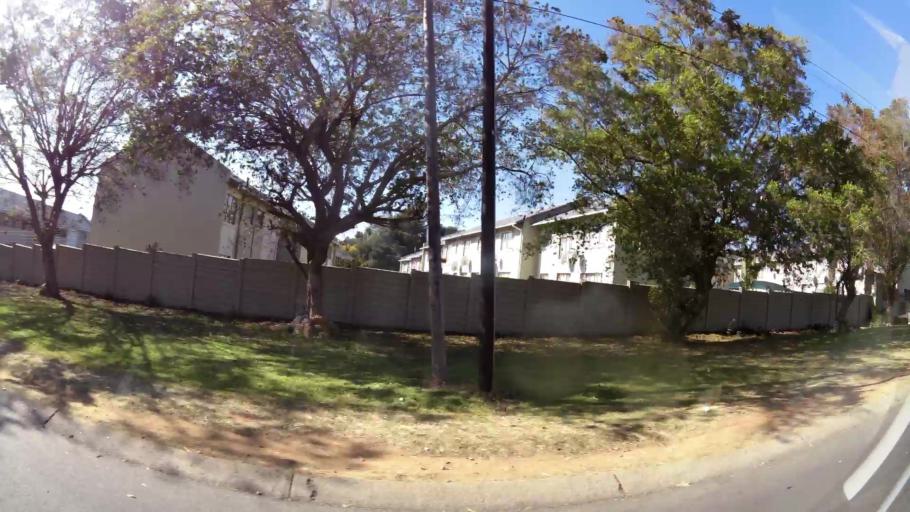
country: ZA
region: Gauteng
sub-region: City of Johannesburg Metropolitan Municipality
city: Modderfontein
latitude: -26.1244
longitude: 28.1045
